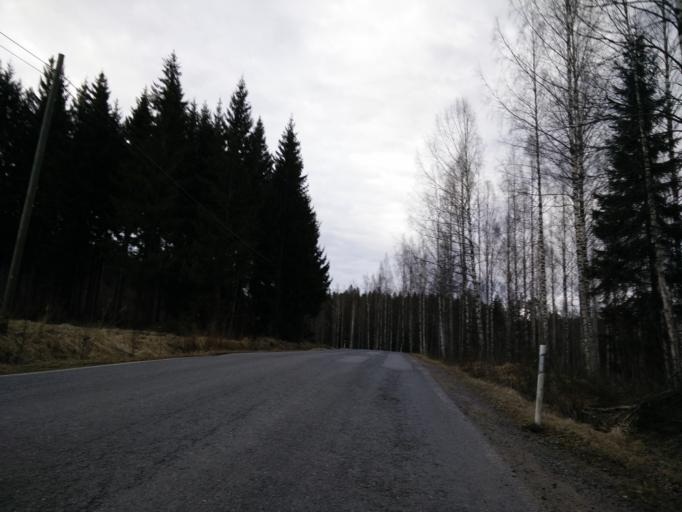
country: FI
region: Pirkanmaa
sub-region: Tampere
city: Orivesi
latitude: 61.6976
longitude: 24.3125
